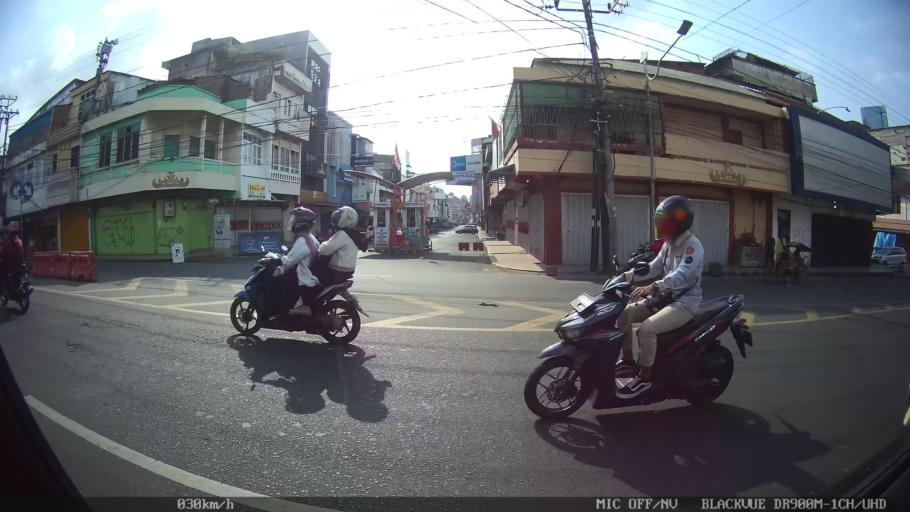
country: ID
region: Lampung
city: Bandarlampung
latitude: -5.4108
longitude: 105.2565
